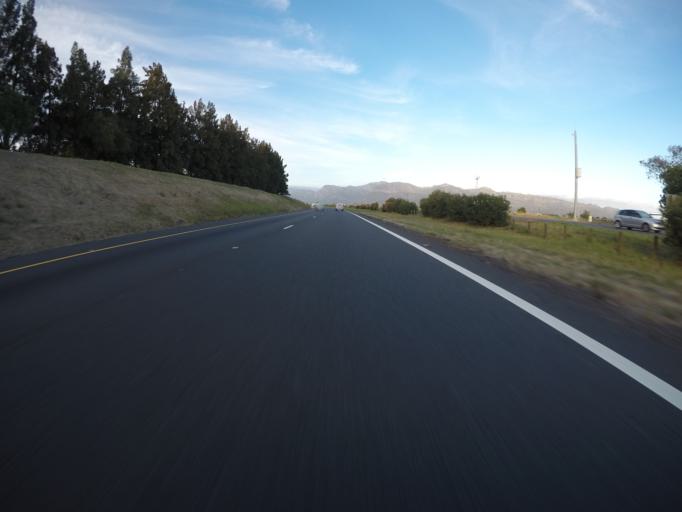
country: ZA
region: Western Cape
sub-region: Cape Winelands District Municipality
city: Paarl
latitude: -33.7842
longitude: 18.9429
